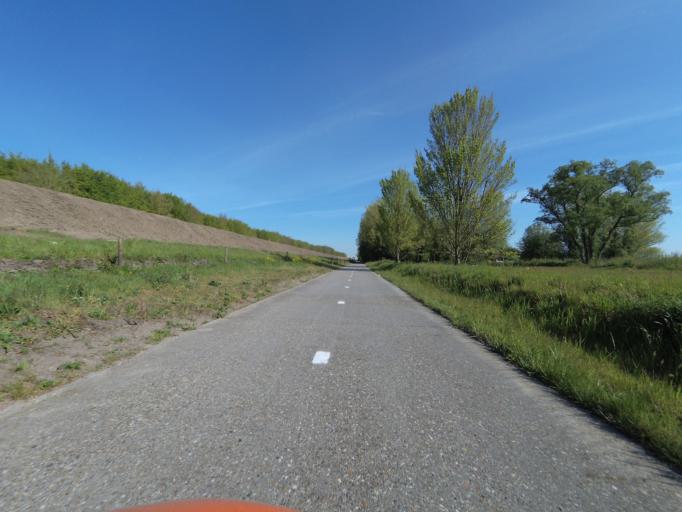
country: NL
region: Overijssel
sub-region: Gemeente Kampen
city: Kampen
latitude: 52.5330
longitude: 5.8549
